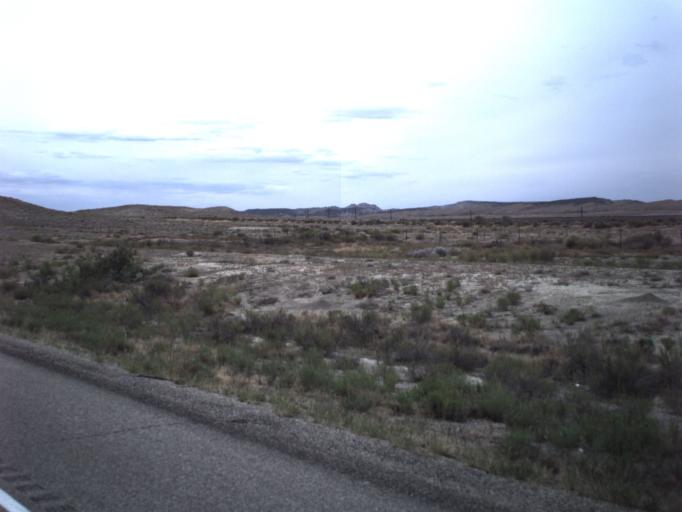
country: US
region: Utah
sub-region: Carbon County
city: East Carbon City
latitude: 39.2513
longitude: -110.3390
